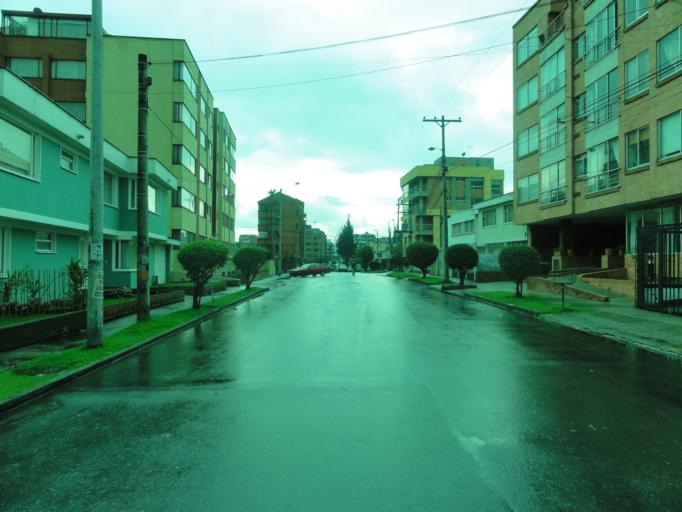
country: CO
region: Bogota D.C.
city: Bogota
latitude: 4.6514
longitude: -74.0793
